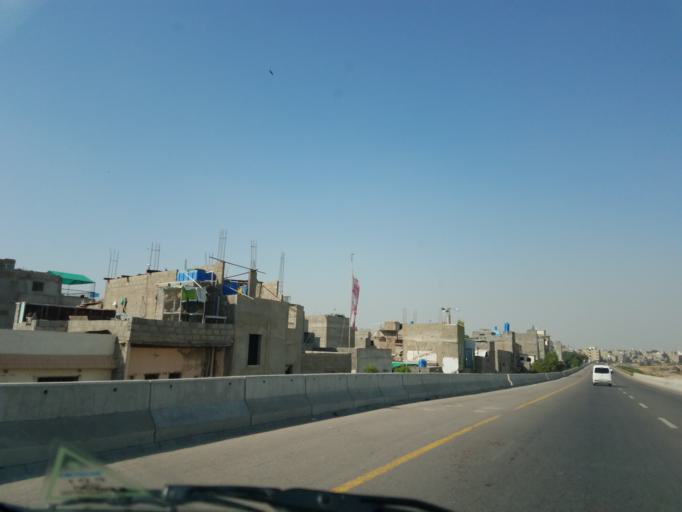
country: PK
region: Sindh
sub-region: Karachi District
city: Karachi
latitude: 24.9179
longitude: 67.0785
